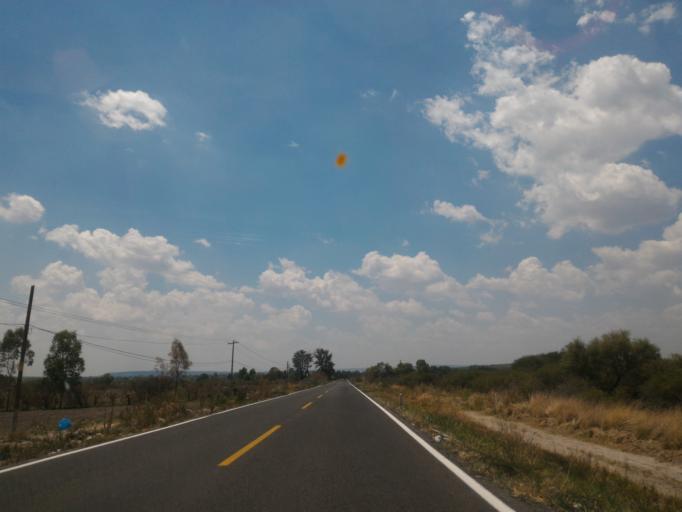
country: MX
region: Guanajuato
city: Ciudad Manuel Doblado
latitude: 20.7819
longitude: -101.9793
